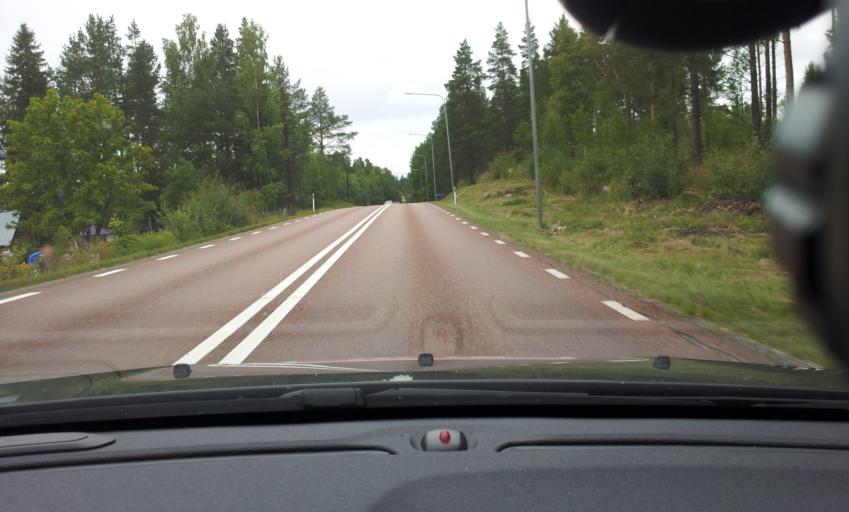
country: SE
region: Jaemtland
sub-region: OEstersunds Kommun
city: Brunflo
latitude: 62.9497
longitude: 15.0515
